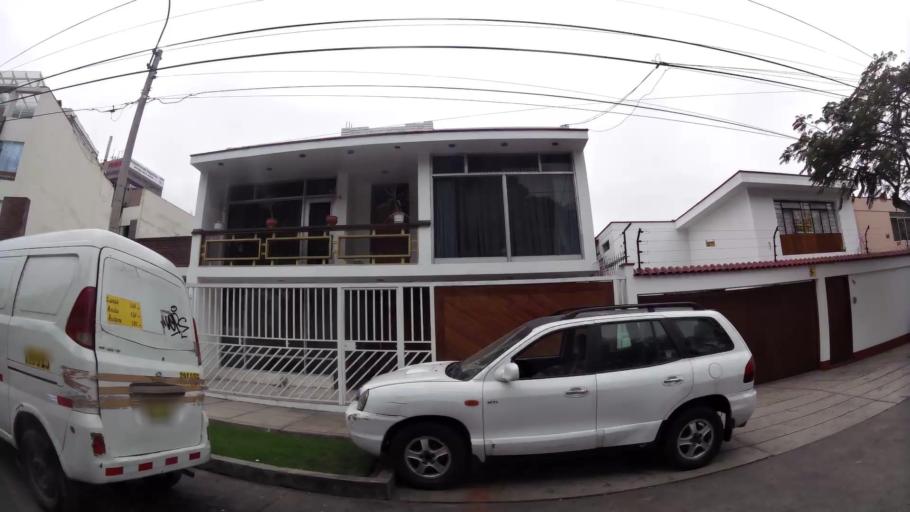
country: PE
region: Lima
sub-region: Lima
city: San Luis
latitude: -12.0996
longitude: -77.0165
